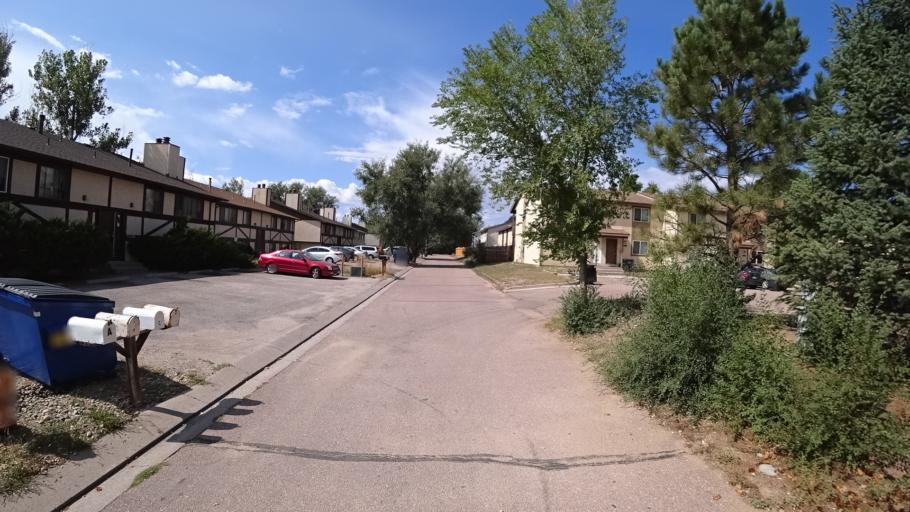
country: US
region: Colorado
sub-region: El Paso County
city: Cimarron Hills
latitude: 38.8583
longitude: -104.7247
